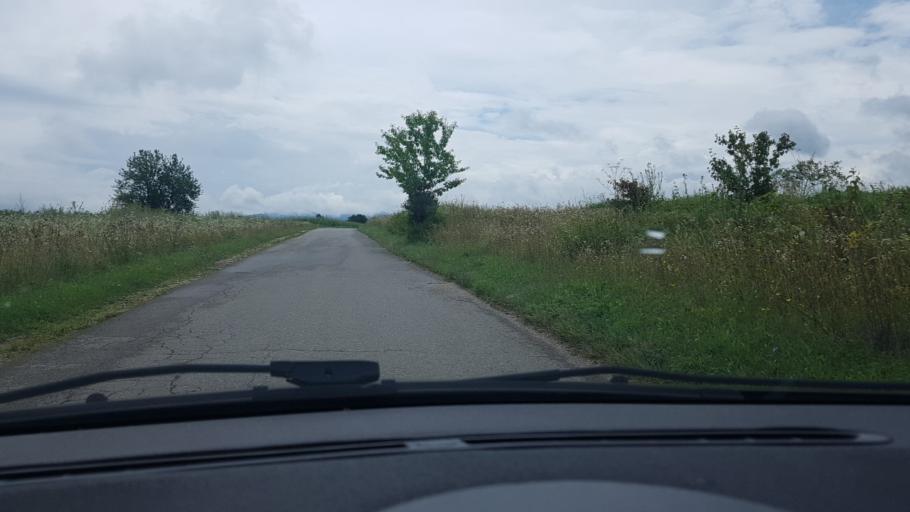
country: BA
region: Federation of Bosnia and Herzegovina
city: Trzacka Rastela
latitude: 44.9627
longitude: 15.6862
